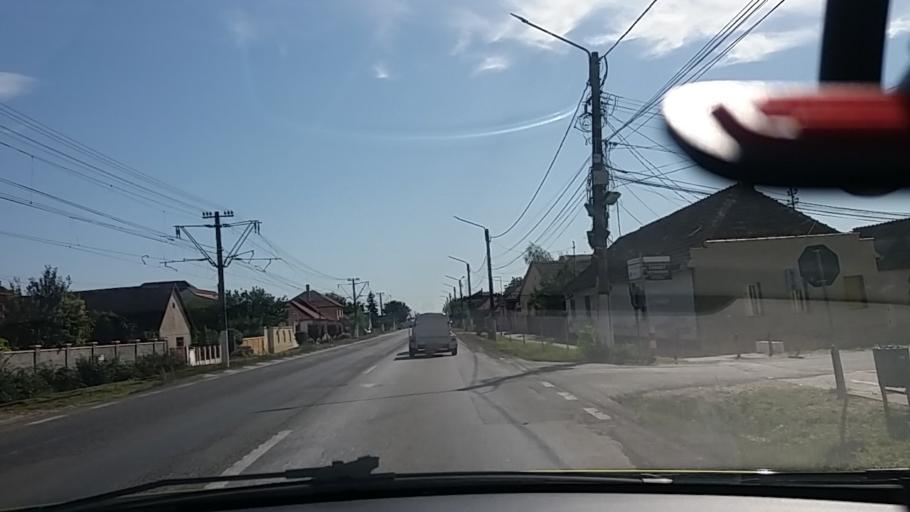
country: RO
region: Arad
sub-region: Comuna Vladimirescu
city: Vladimirescu
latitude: 46.1631
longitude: 21.4065
